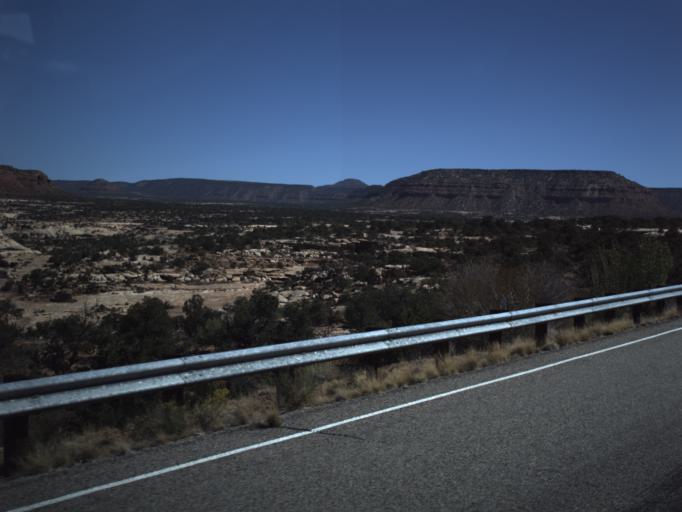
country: US
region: Utah
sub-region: San Juan County
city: Blanding
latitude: 37.6524
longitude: -110.1288
